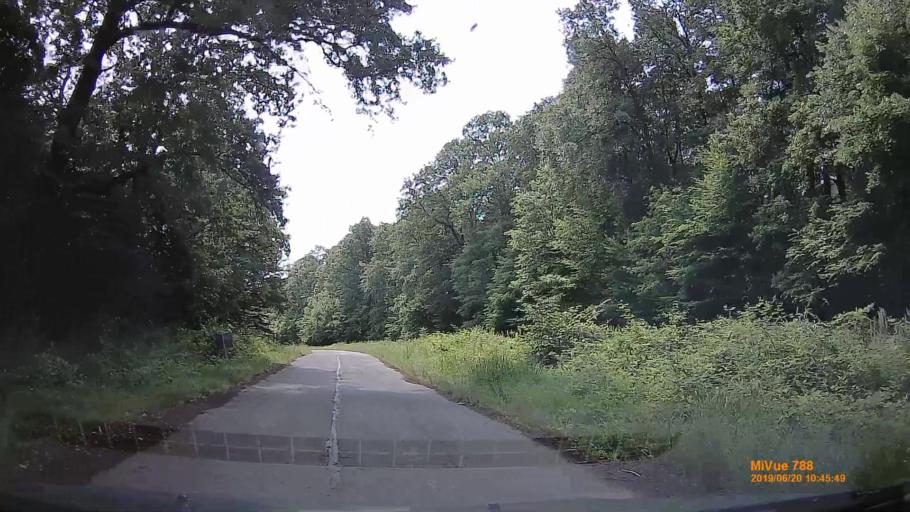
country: HU
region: Baranya
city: Hidas
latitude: 46.1812
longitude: 18.5735
